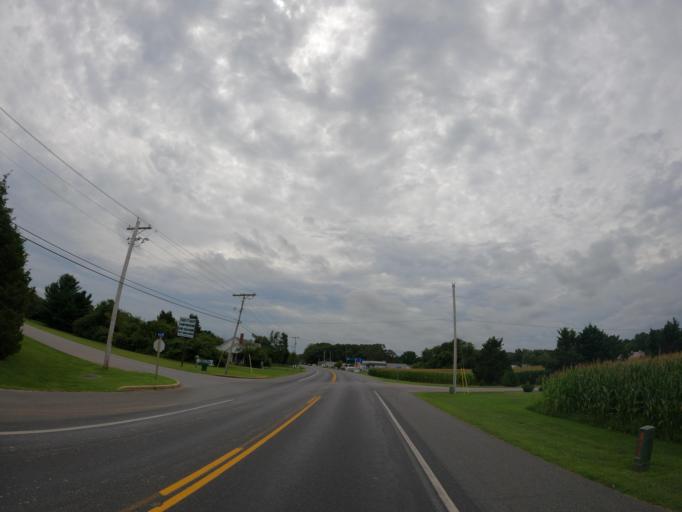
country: US
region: Maryland
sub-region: Saint Mary's County
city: California
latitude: 38.2269
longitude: -76.5190
